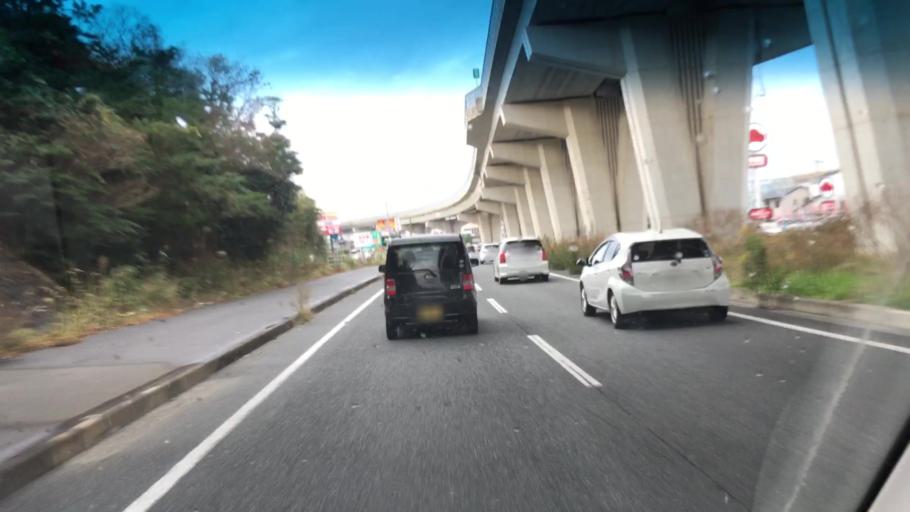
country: JP
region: Fukuoka
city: Maebaru-chuo
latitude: 33.5734
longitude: 130.2665
